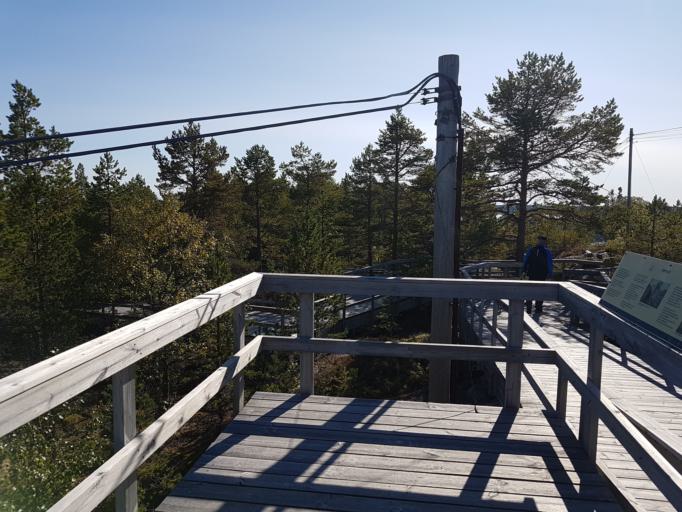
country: SE
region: Vaesterbotten
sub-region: Skelleftea Kommun
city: Skelleftehamn
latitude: 64.4807
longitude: 21.5754
